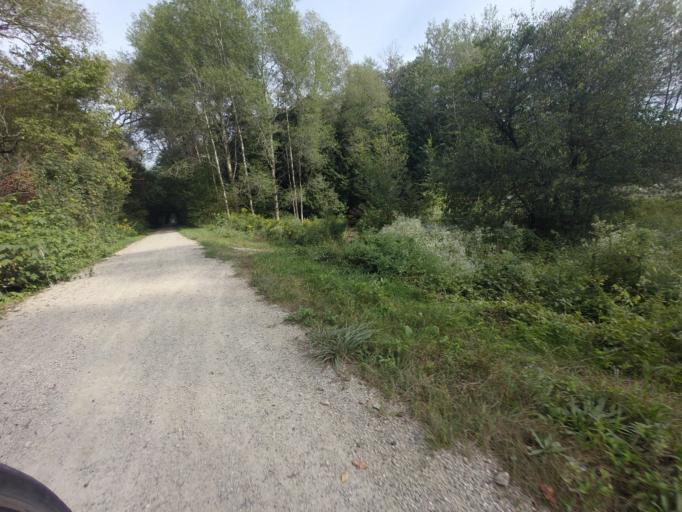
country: CA
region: Ontario
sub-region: Wellington County
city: Guelph
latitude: 43.5691
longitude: -80.3296
